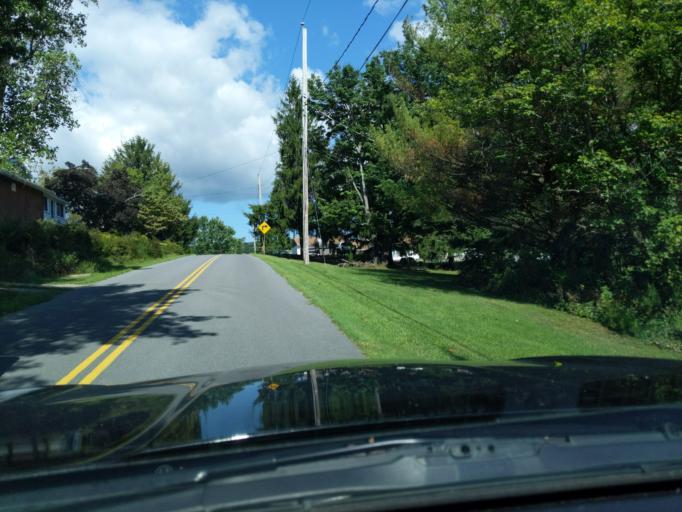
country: US
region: Pennsylvania
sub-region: Blair County
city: Altoona
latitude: 40.5411
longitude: -78.3978
